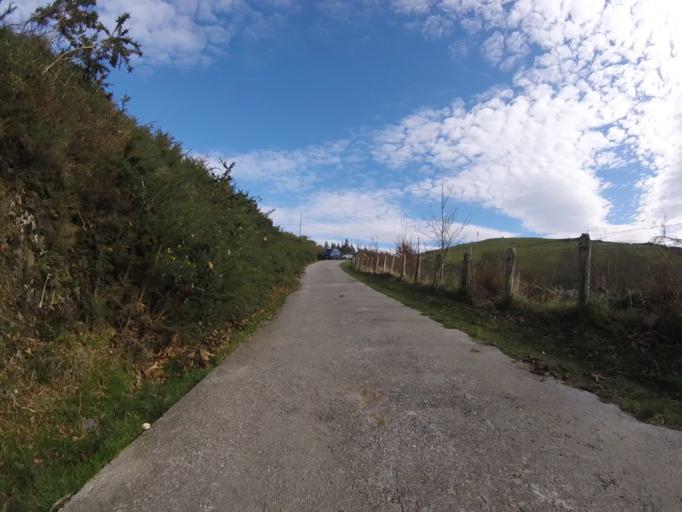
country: ES
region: Navarre
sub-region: Provincia de Navarra
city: Arano
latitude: 43.2414
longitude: -1.8418
